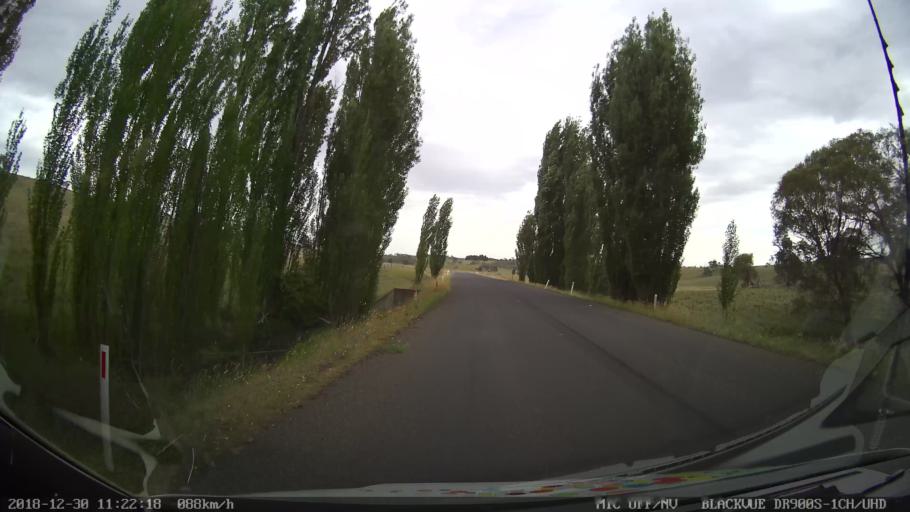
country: AU
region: New South Wales
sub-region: Snowy River
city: Jindabyne
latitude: -36.5014
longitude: 148.6708
